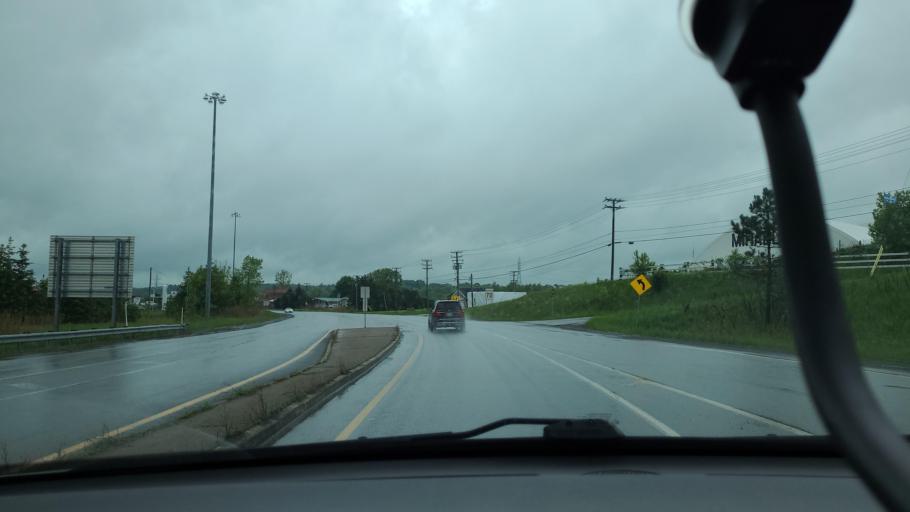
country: CA
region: Quebec
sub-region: Laurentides
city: Saint-Jerome
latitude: 45.7464
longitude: -74.0085
